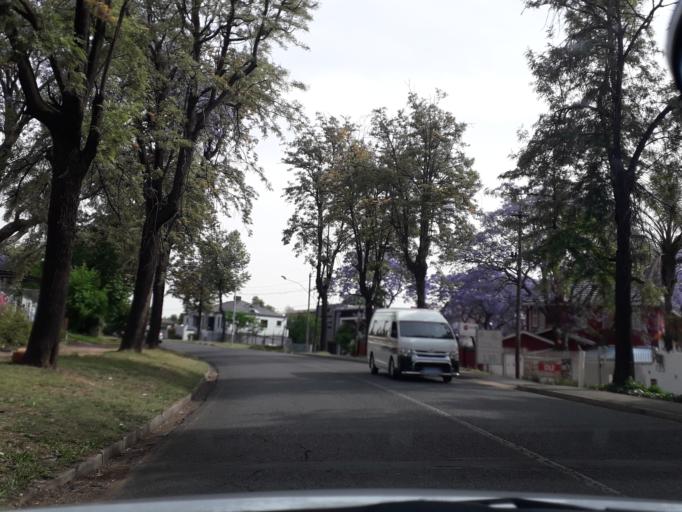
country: ZA
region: Gauteng
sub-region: City of Johannesburg Metropolitan Municipality
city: Johannesburg
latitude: -26.1519
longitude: 28.0331
